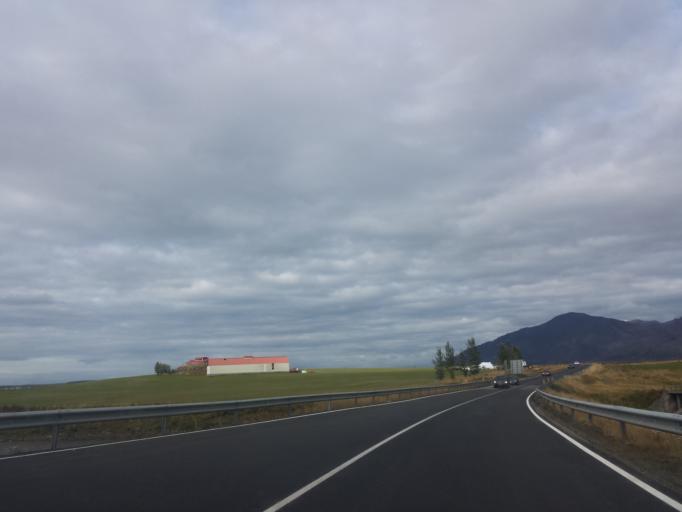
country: IS
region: West
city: Borgarnes
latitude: 64.3891
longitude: -21.8487
